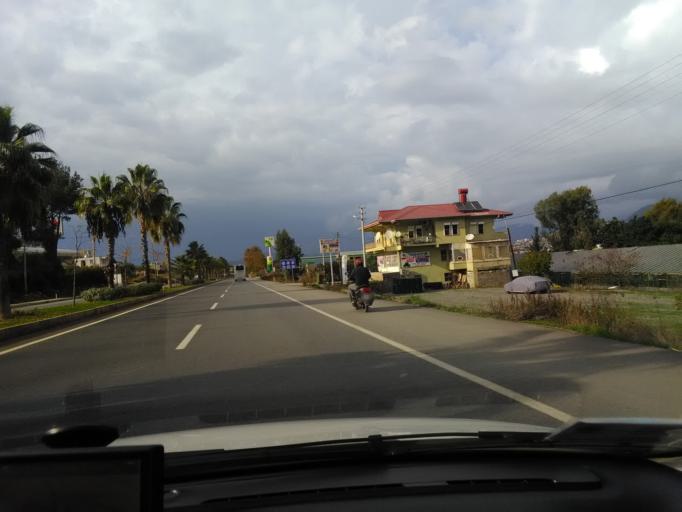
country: TR
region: Antalya
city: Gazipasa
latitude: 36.2504
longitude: 32.3396
